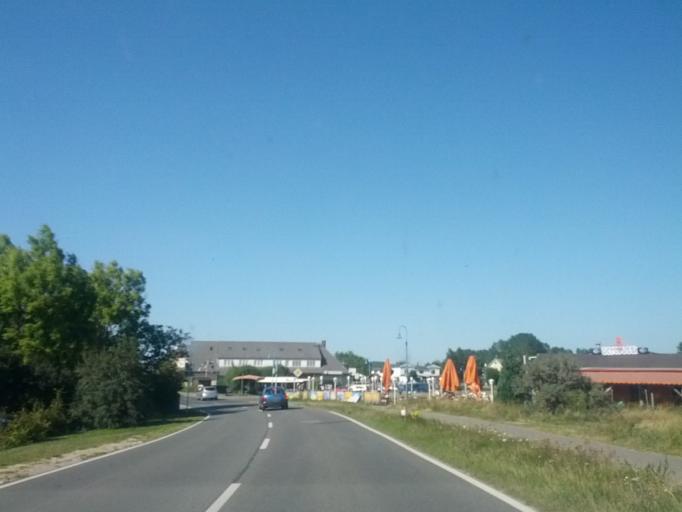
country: DE
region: Mecklenburg-Vorpommern
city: Ostseebad Gohren
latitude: 54.3162
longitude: 13.7204
